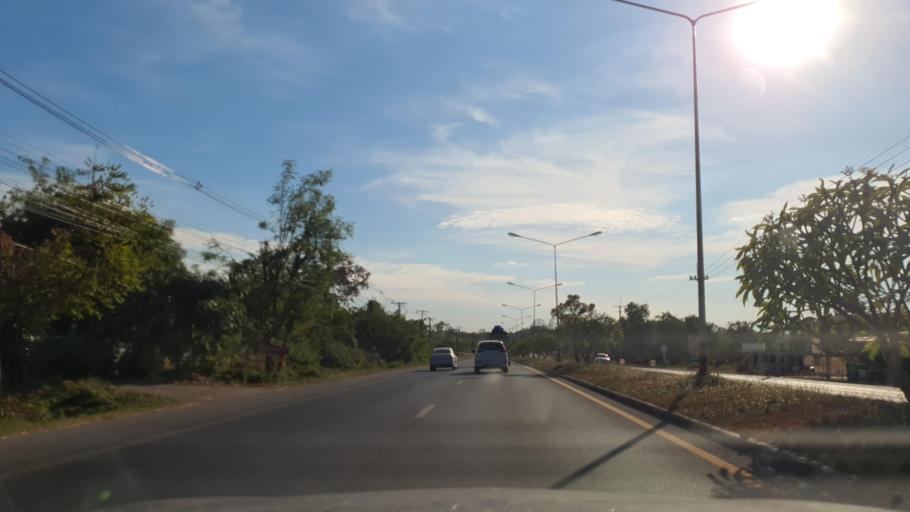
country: TH
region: Kalasin
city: Yang Talat
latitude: 16.3669
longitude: 103.3426
